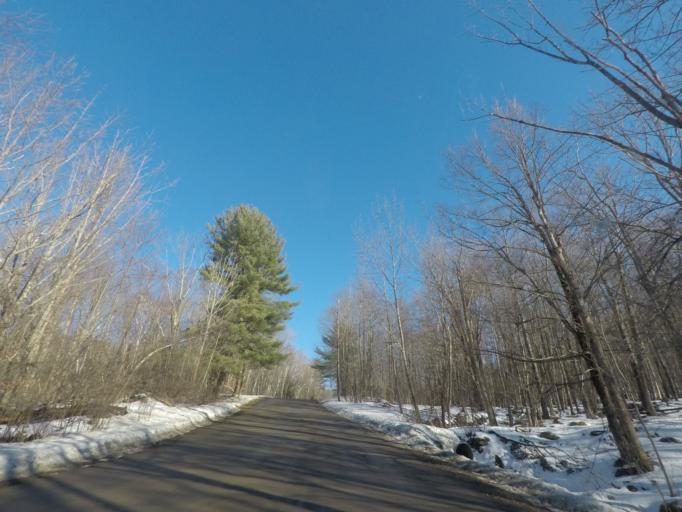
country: US
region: New York
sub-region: Rensselaer County
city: Averill Park
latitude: 42.6400
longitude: -73.5147
